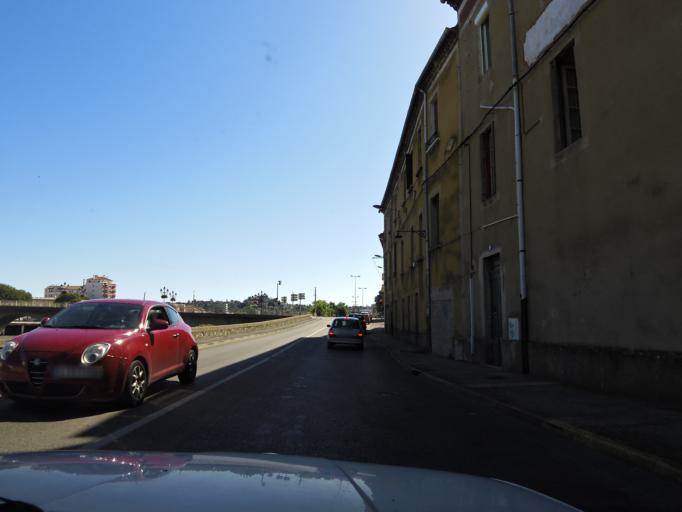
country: FR
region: Languedoc-Roussillon
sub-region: Departement du Gard
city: Ales
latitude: 44.1205
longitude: 4.0778
